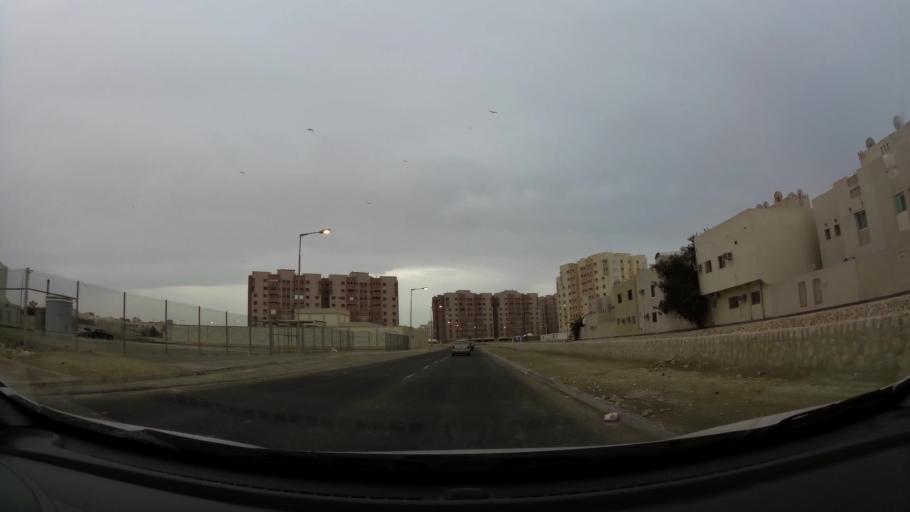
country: BH
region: Central Governorate
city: Madinat Hamad
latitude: 26.1232
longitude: 50.4882
